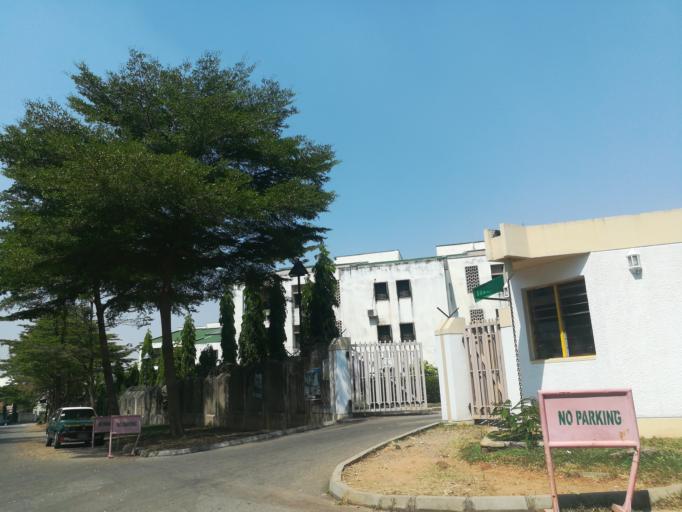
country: NG
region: Abuja Federal Capital Territory
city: Abuja
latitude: 9.0751
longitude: 7.4513
